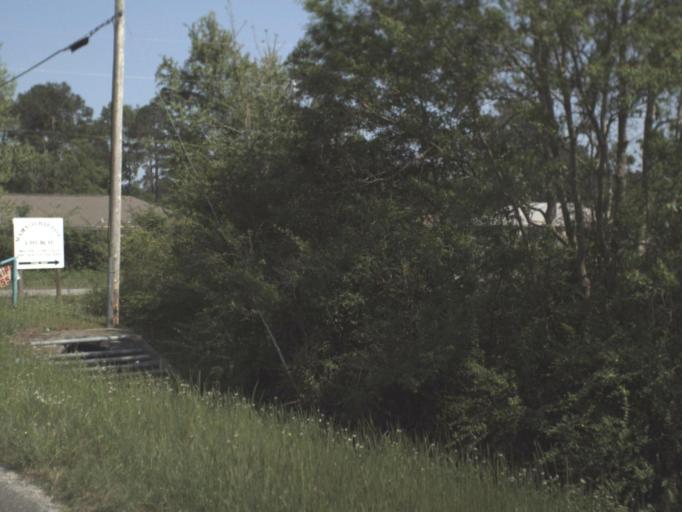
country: US
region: Florida
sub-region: Escambia County
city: Myrtle Grove
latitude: 30.4210
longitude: -87.3233
